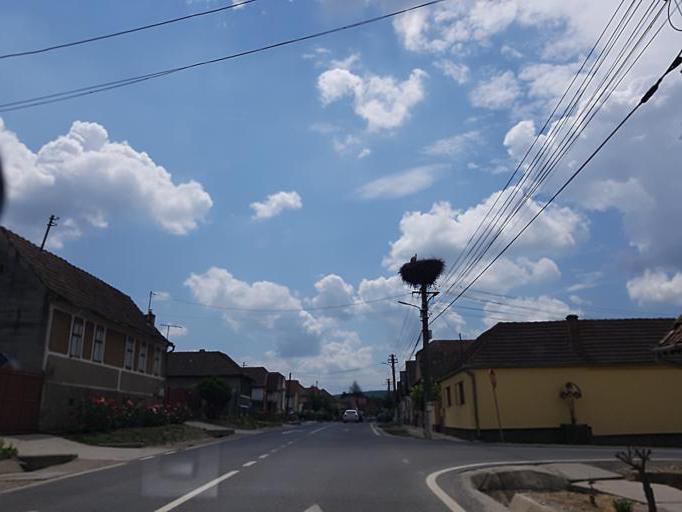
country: RO
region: Sibiu
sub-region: Comuna Slimnic
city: Slimnic
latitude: 45.9187
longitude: 24.1552
